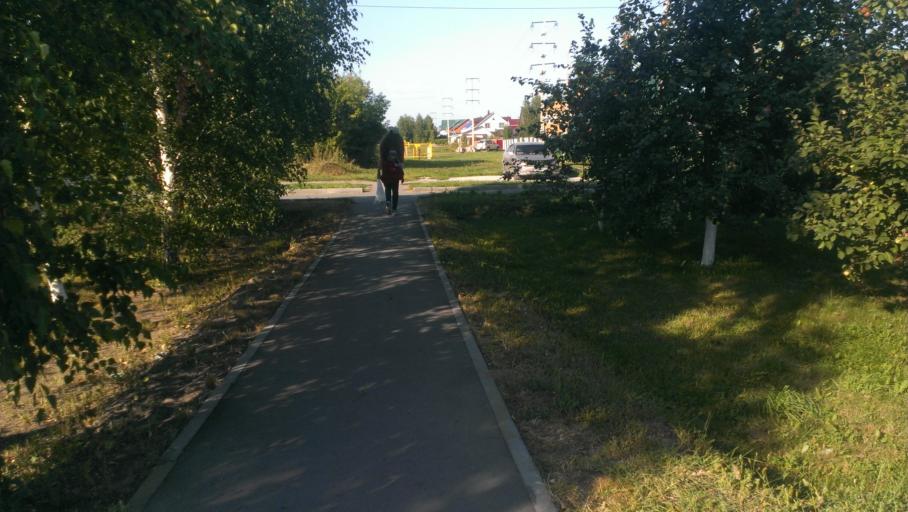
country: RU
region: Altai Krai
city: Novosilikatnyy
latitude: 53.3580
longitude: 83.6385
